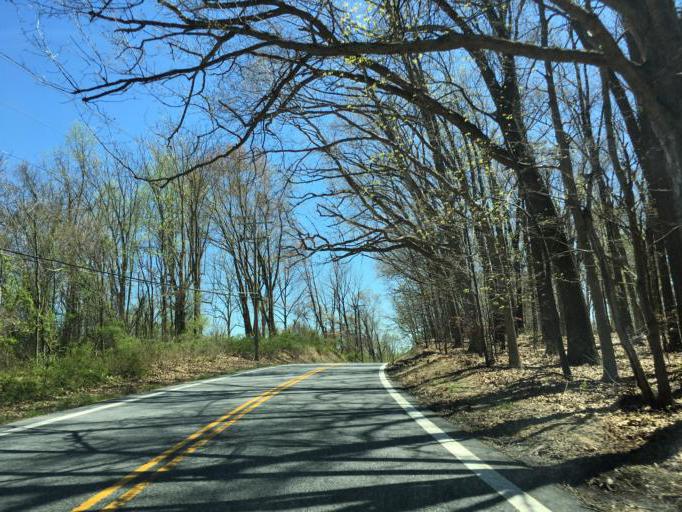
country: US
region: Maryland
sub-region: Baltimore County
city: Hunt Valley
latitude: 39.5857
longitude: -76.6314
